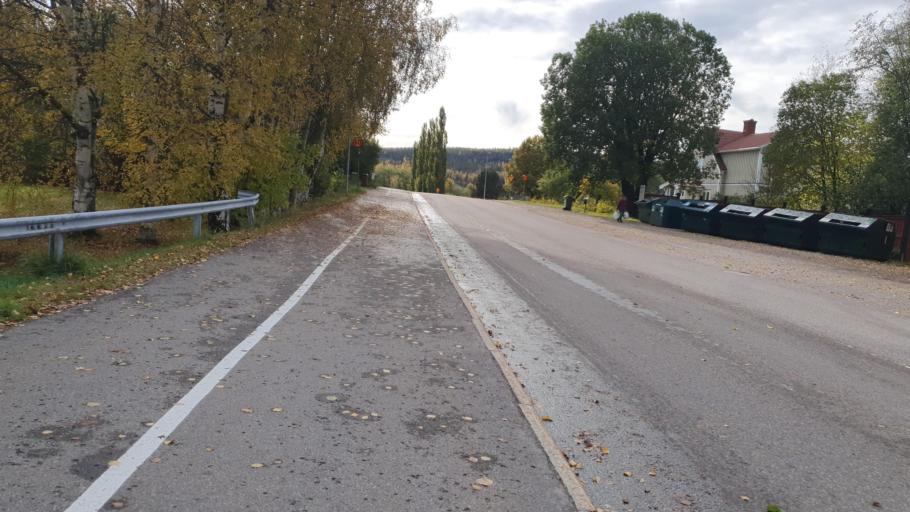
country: SE
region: Vaesternorrland
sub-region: Sundsvalls Kommun
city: Sundsvall
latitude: 62.4060
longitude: 17.2451
